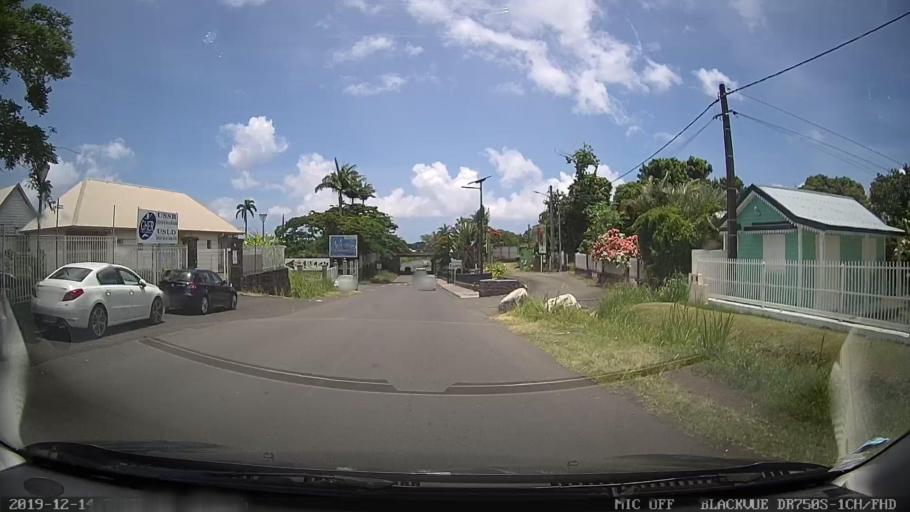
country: RE
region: Reunion
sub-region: Reunion
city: Saint-Andre
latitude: -20.9538
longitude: 55.6553
